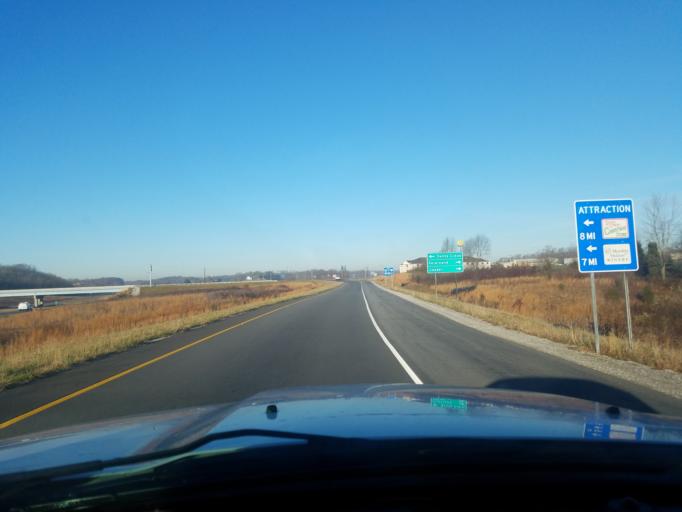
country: US
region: Indiana
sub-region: Dubois County
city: Ferdinand
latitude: 38.2062
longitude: -86.8631
